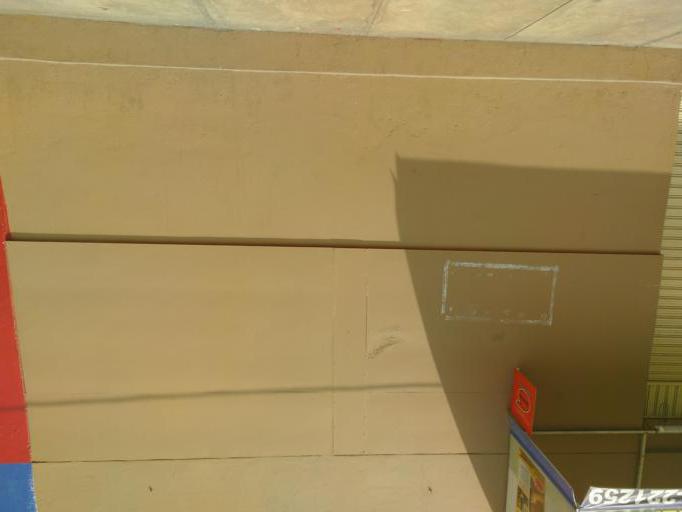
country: PE
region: Arequipa
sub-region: Provincia de Arequipa
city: Arequipa
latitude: -16.4085
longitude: -71.5397
